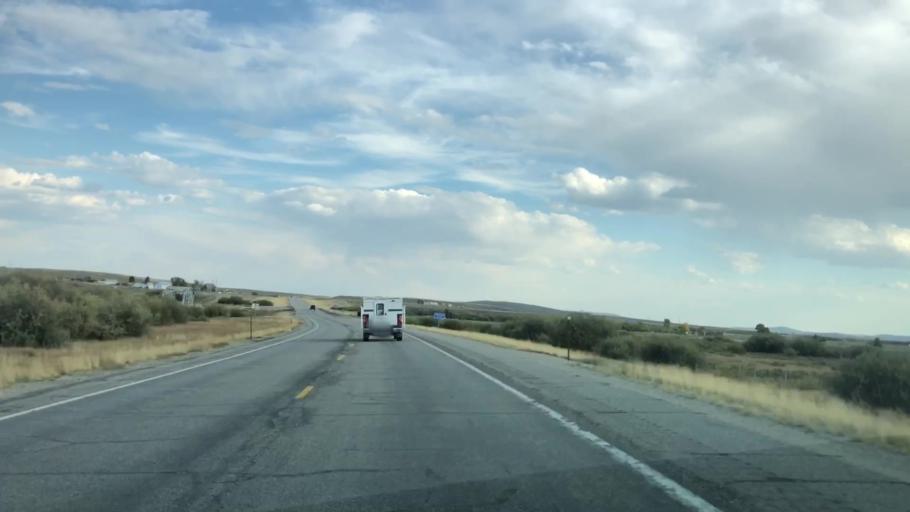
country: US
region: Wyoming
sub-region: Sublette County
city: Pinedale
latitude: 43.0208
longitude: -110.1215
